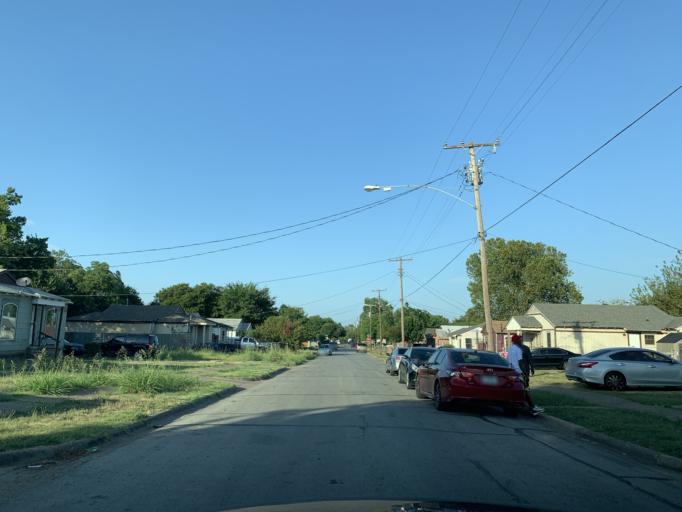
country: US
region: Texas
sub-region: Dallas County
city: Dallas
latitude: 32.7072
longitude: -96.7959
